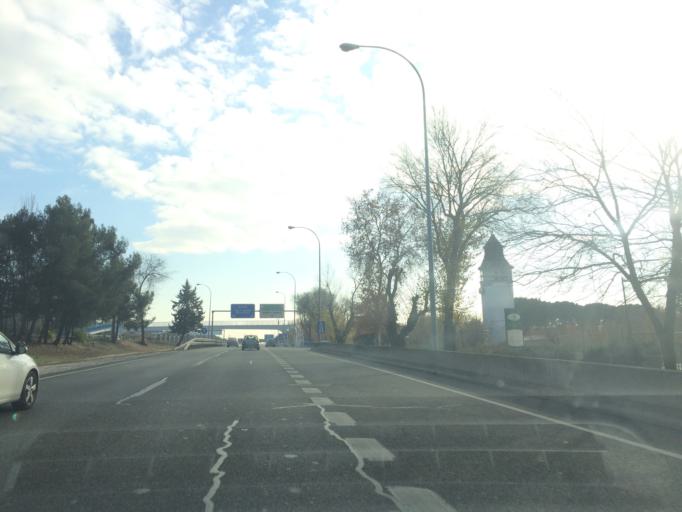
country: ES
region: Madrid
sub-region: Provincia de Madrid
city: Fuencarral-El Pardo
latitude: 40.4729
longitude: -3.7513
